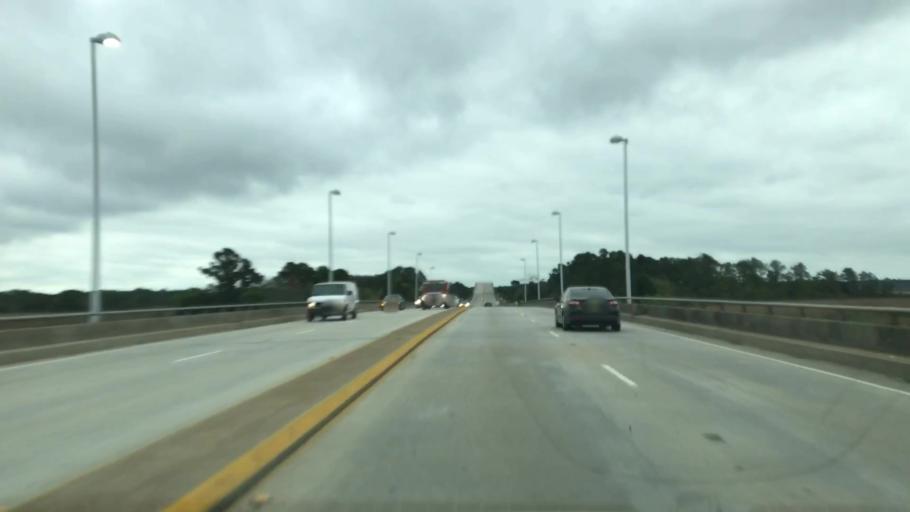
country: US
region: South Carolina
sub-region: Georgetown County
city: Georgetown
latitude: 33.3669
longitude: -79.2653
